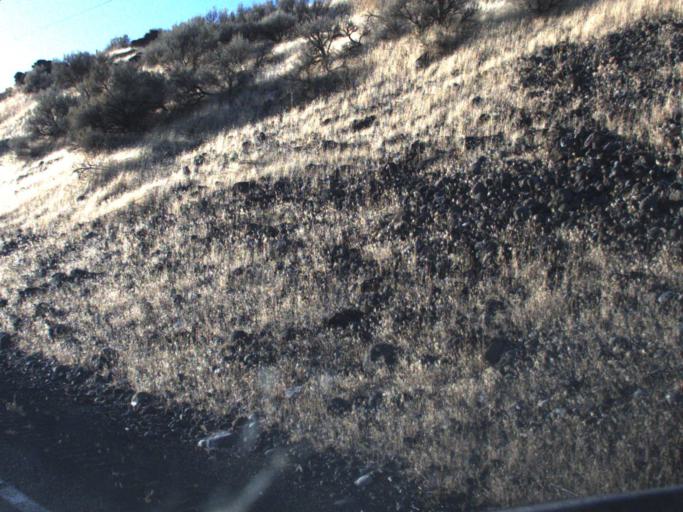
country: US
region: Washington
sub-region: Franklin County
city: Connell
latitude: 46.6504
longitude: -118.5099
